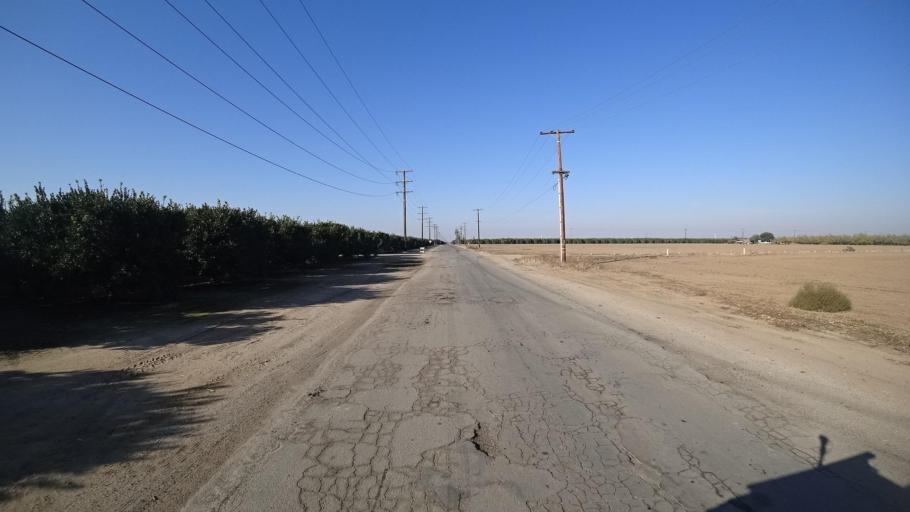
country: US
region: California
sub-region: Tulare County
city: Richgrove
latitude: 35.7327
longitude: -119.1315
